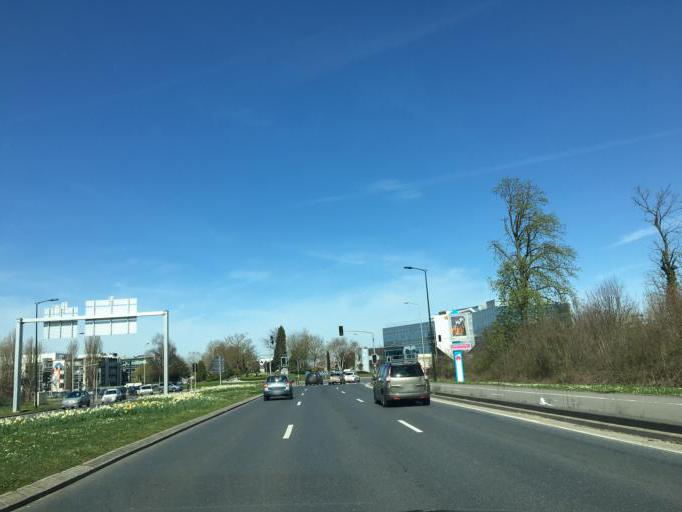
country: FR
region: Ile-de-France
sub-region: Departement de l'Essonne
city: Evry
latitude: 48.6191
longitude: 2.4528
